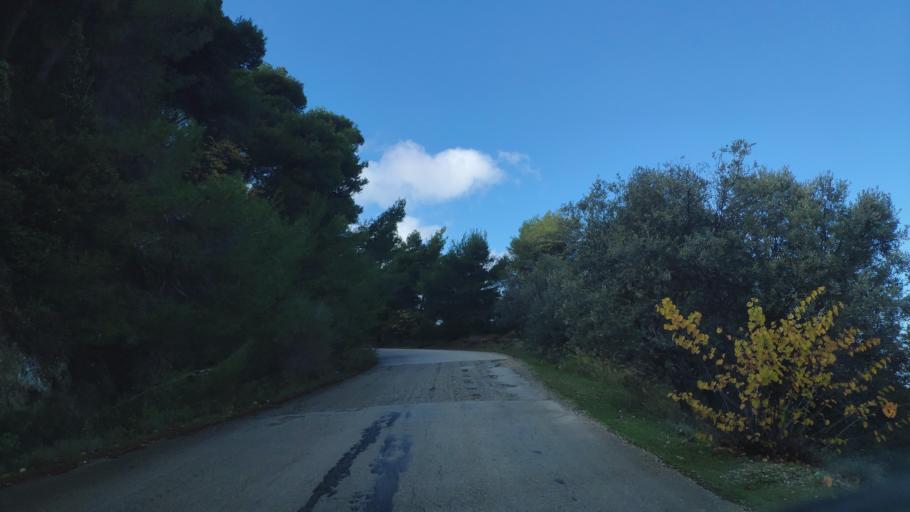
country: GR
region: West Greece
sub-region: Nomos Achaias
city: Aiyira
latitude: 38.1007
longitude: 22.4453
